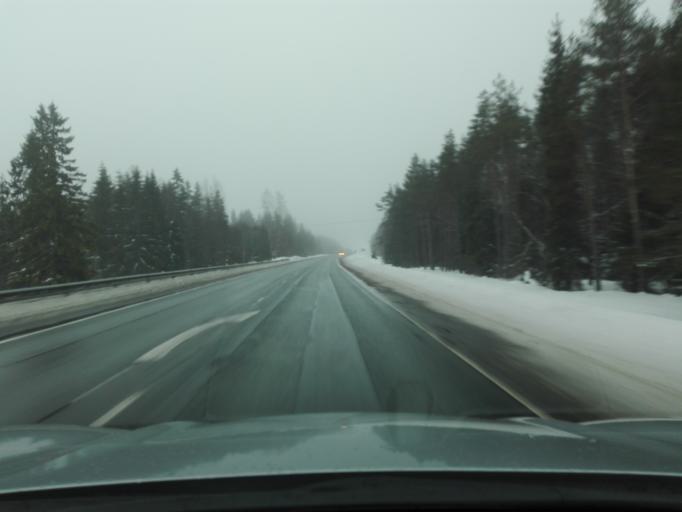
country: EE
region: Raplamaa
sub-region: Kohila vald
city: Kohila
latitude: 59.1876
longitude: 24.7866
